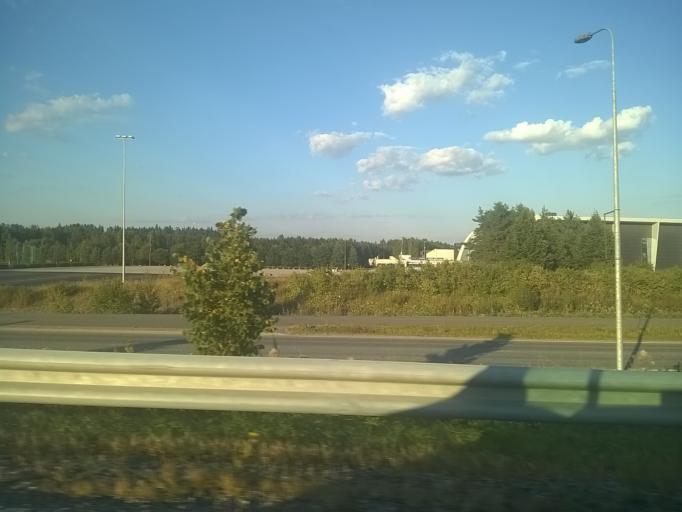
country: FI
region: Pirkanmaa
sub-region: Tampere
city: Tampere
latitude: 61.4645
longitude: 23.7262
